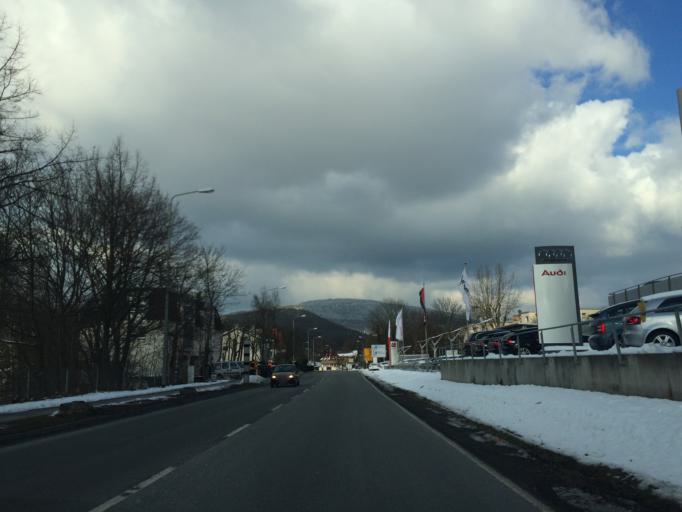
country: DE
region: Hesse
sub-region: Regierungsbezirk Darmstadt
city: Konigstein im Taunus
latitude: 50.1769
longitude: 8.4750
